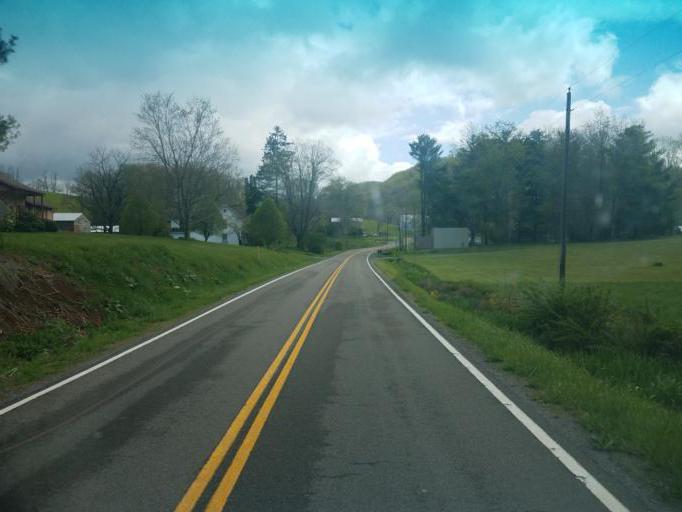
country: US
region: Virginia
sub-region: Wythe County
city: Rural Retreat
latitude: 37.0175
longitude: -81.3459
